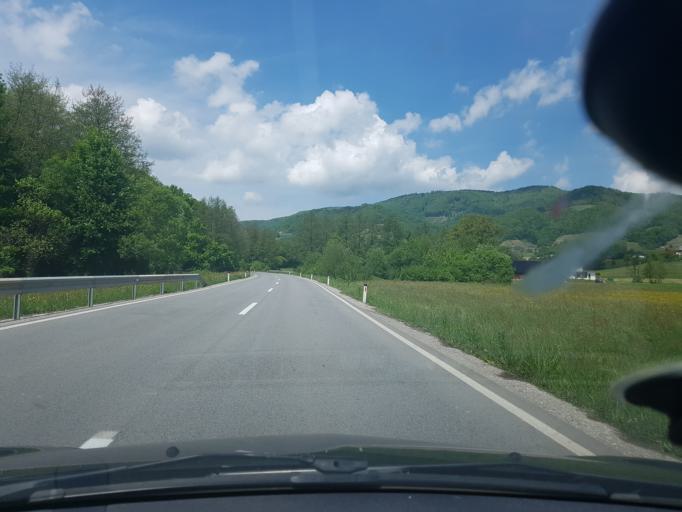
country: SI
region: Rogaska Slatina
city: Rogaska Slatina
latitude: 46.2450
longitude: 15.6528
